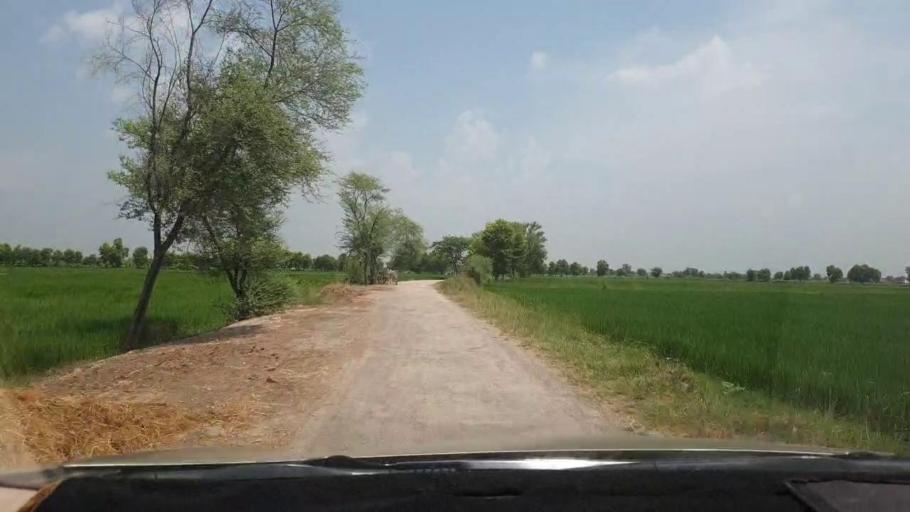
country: PK
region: Sindh
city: Naudero
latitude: 27.7343
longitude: 68.3437
